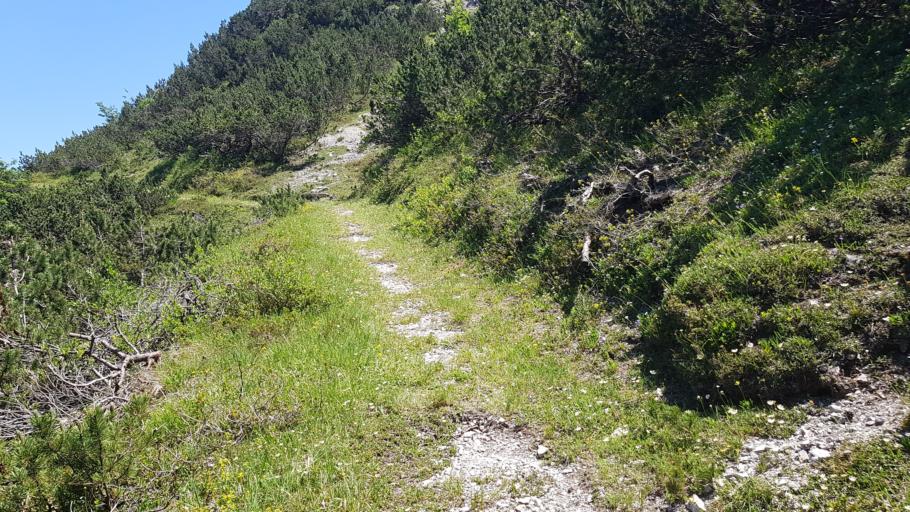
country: IT
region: Friuli Venezia Giulia
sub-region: Provincia di Udine
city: Paularo
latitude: 46.4859
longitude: 13.1561
